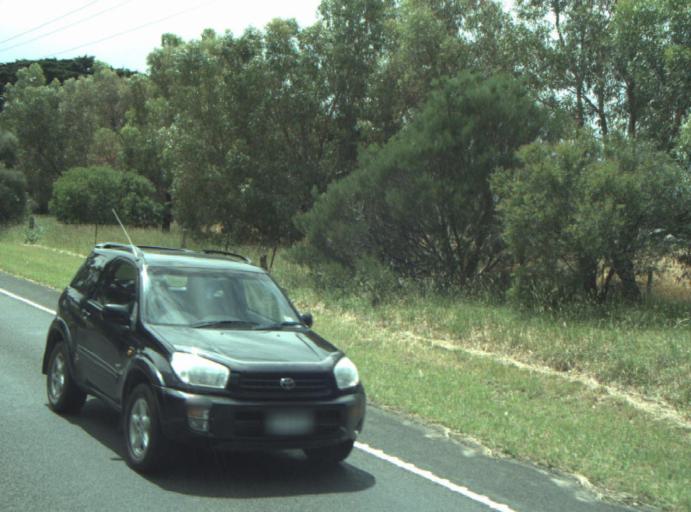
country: AU
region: Victoria
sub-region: Greater Geelong
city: Wandana Heights
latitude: -38.2321
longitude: 144.2797
